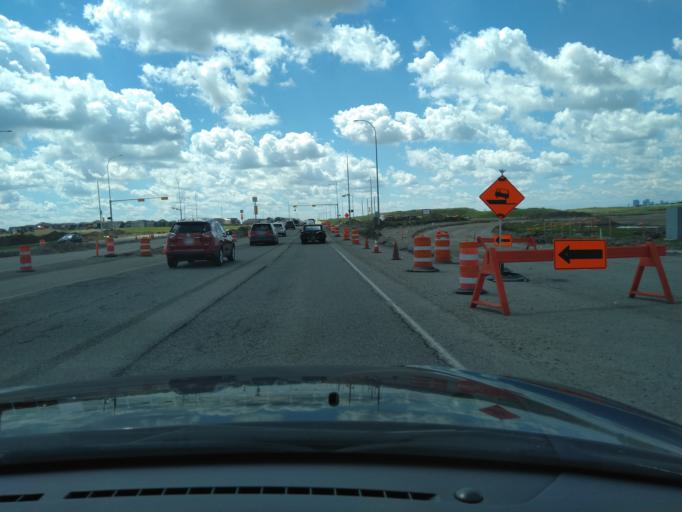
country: CA
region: Alberta
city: Calgary
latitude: 51.1410
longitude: -113.9703
